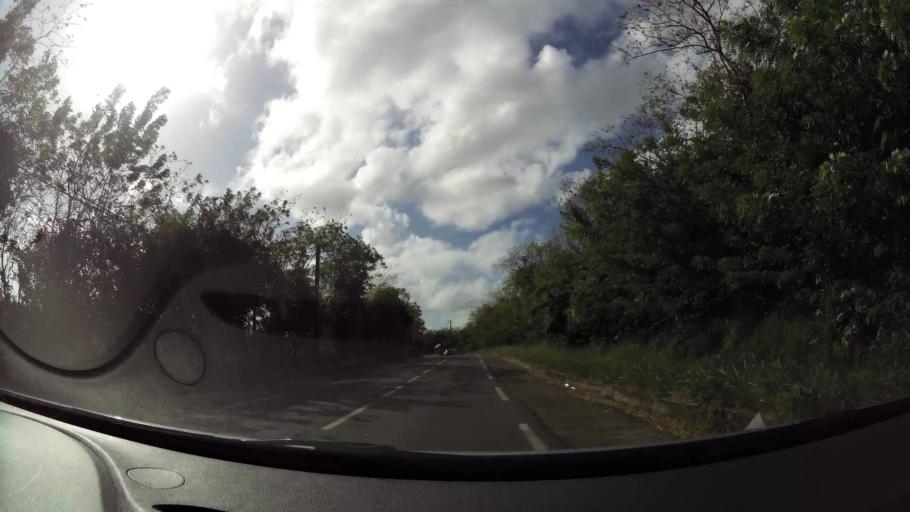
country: MQ
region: Martinique
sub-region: Martinique
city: Le Vauclin
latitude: 14.5710
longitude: -60.8590
